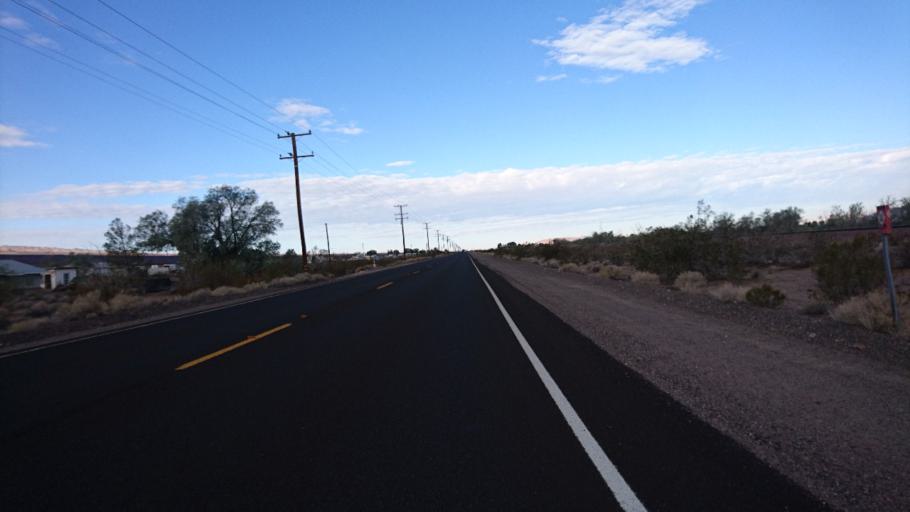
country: US
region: California
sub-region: San Bernardino County
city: Barstow
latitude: 34.8412
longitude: -116.7465
